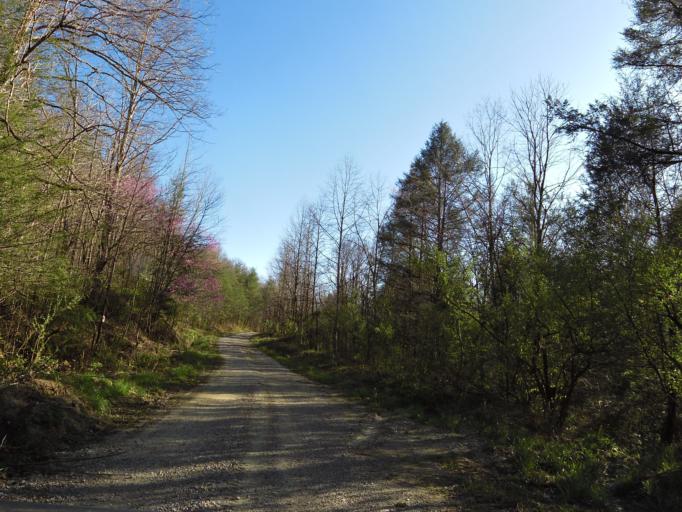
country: US
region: Tennessee
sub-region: Roane County
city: Oliver Springs
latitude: 36.2086
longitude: -84.4160
